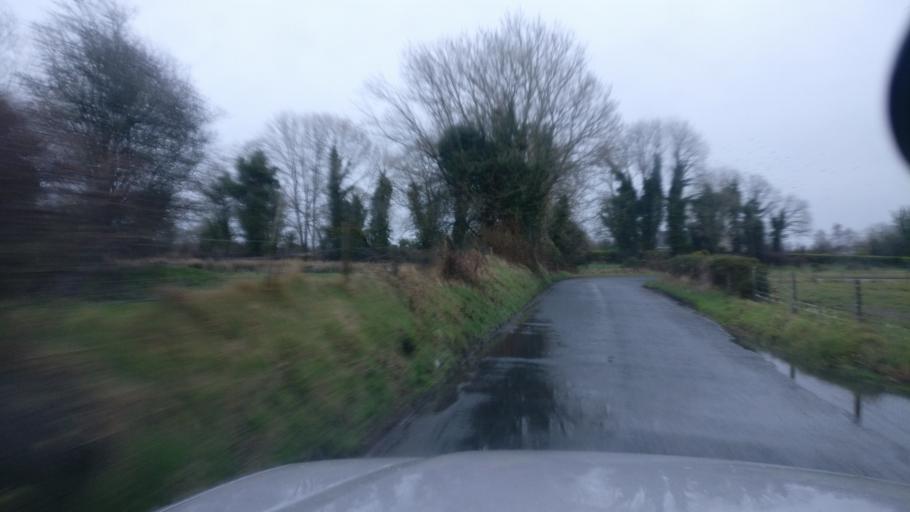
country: IE
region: Connaught
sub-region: County Galway
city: Ballinasloe
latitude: 53.3275
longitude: -8.3906
